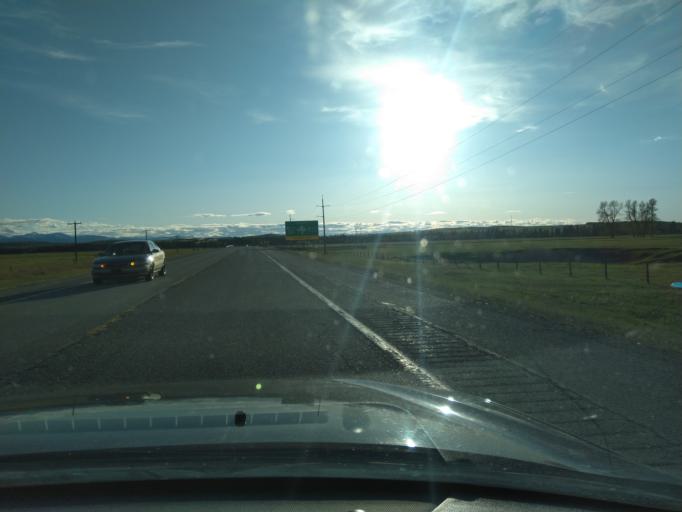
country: CA
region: Alberta
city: Cochrane
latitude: 51.0235
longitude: -114.4517
